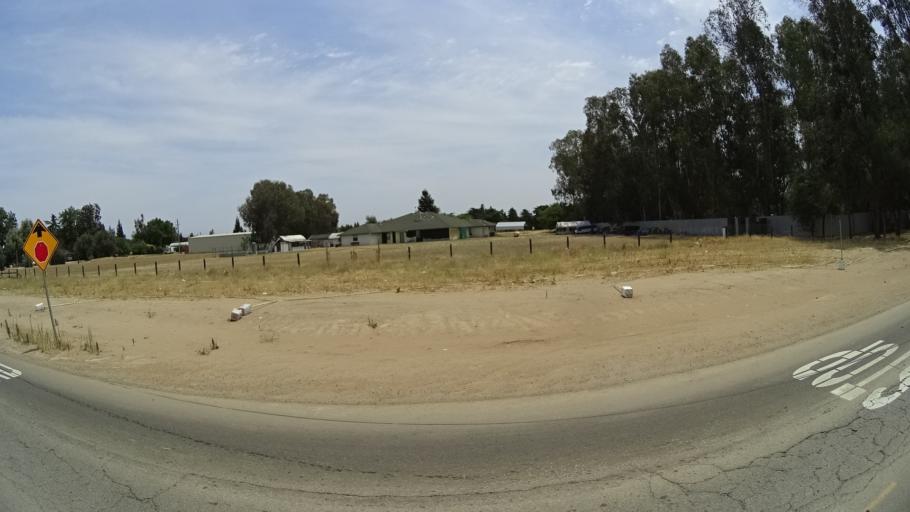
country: US
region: California
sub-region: Fresno County
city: Sunnyside
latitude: 36.7486
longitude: -119.6643
